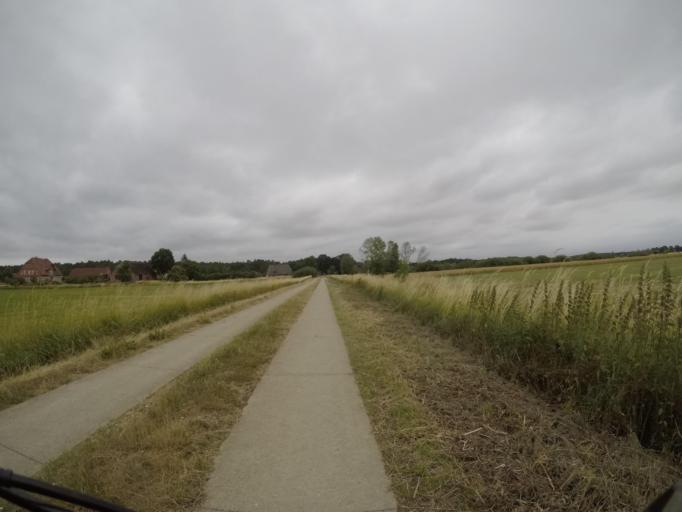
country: DE
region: Lower Saxony
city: Hitzacker
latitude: 53.1793
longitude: 11.0841
